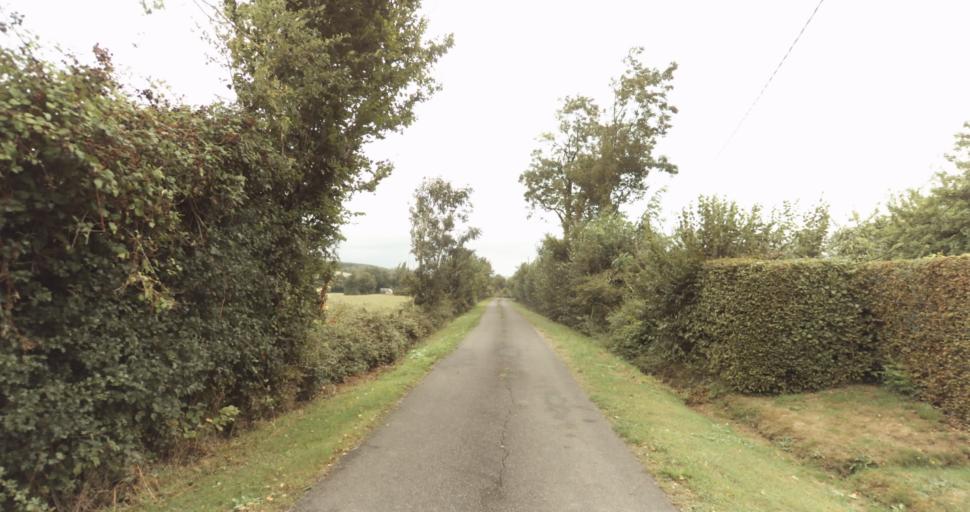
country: FR
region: Lower Normandy
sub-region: Departement de l'Orne
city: Sainte-Gauburge-Sainte-Colombe
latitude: 48.7006
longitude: 0.4477
